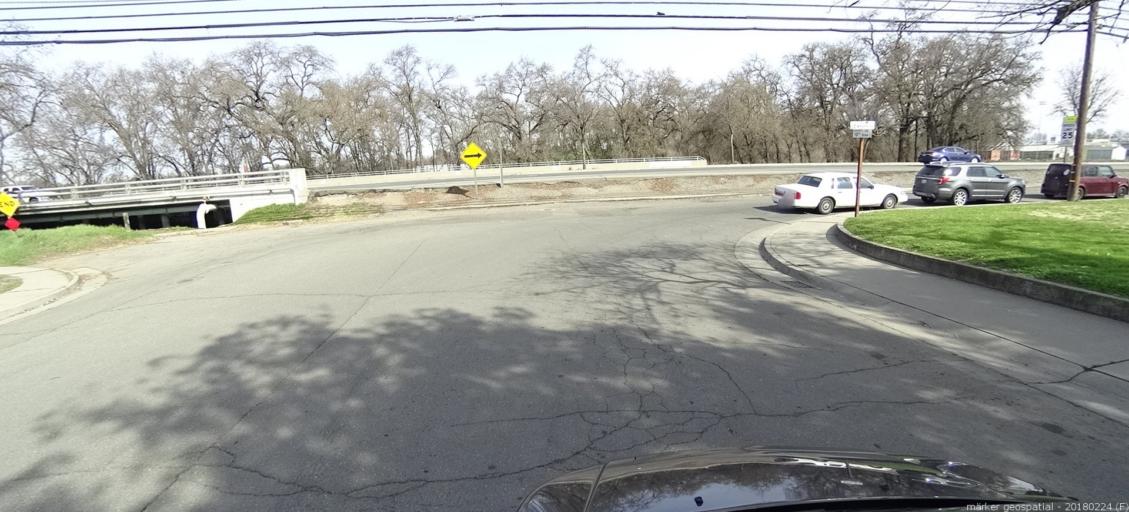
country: US
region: California
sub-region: Sacramento County
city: Rio Linda
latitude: 38.6835
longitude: -121.4431
